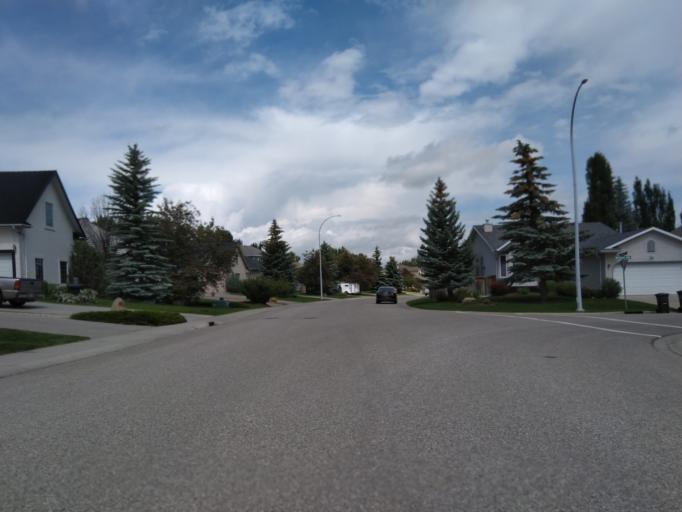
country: CA
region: Alberta
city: Cochrane
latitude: 51.1859
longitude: -114.4991
